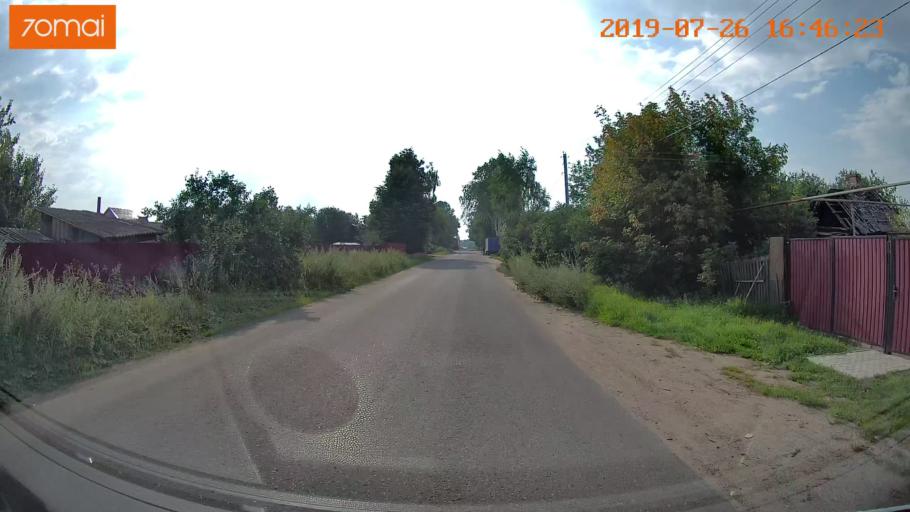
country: RU
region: Ivanovo
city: Bogorodskoye
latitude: 57.0448
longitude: 41.0182
